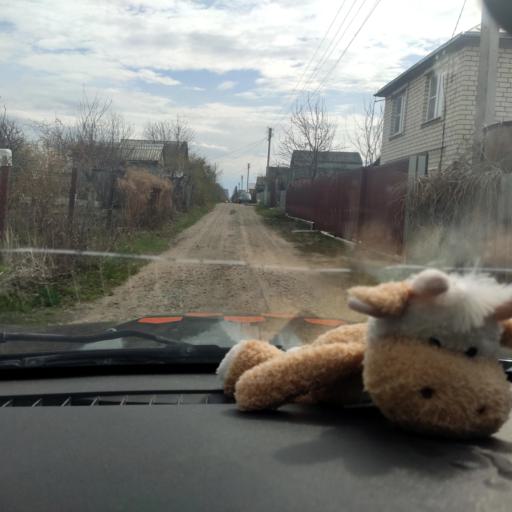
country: RU
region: Samara
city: Tol'yatti
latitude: 53.6034
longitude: 49.2423
